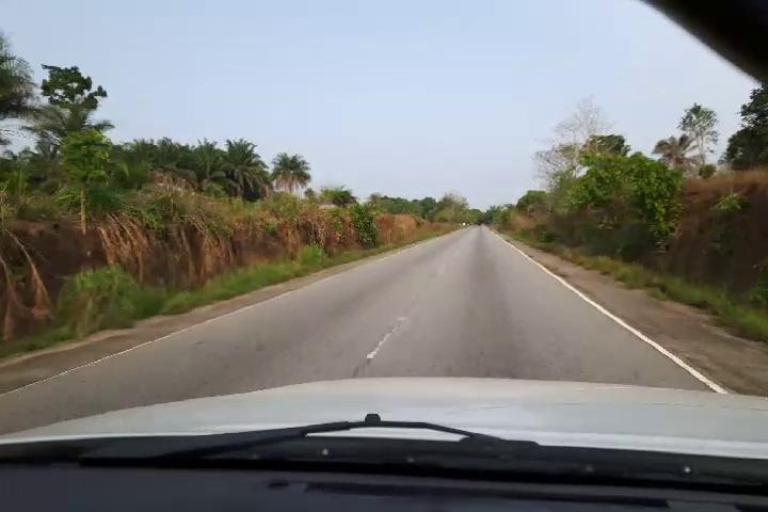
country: SL
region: Eastern Province
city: Blama
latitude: 7.9389
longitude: -11.4931
